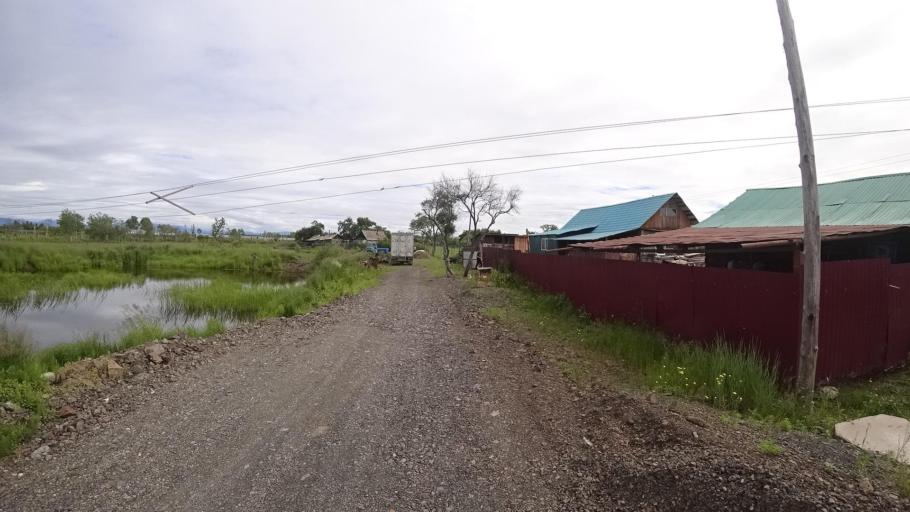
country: RU
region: Khabarovsk Krai
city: Amursk
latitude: 49.9008
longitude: 136.1490
